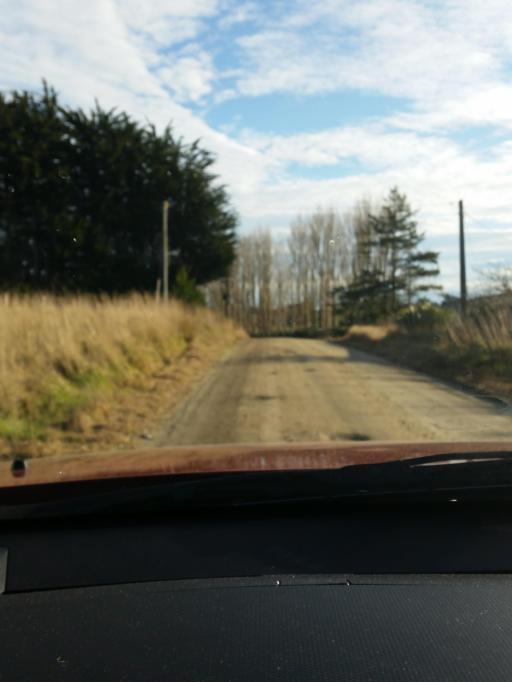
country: NZ
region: Southland
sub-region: Gore District
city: Gore
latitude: -46.2056
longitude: 168.7741
